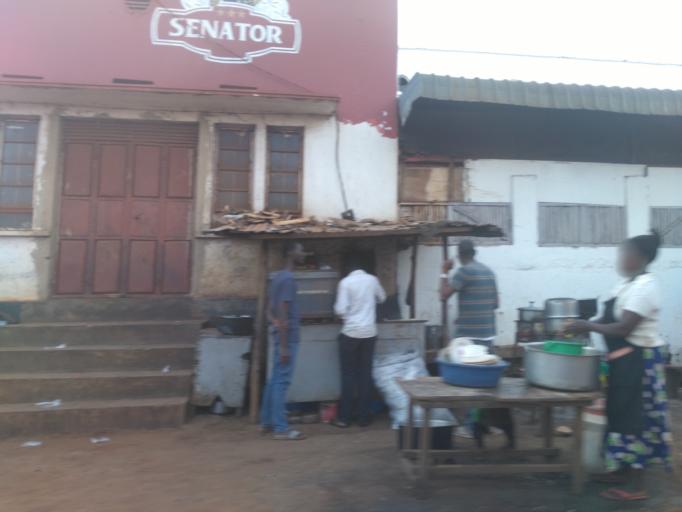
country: UG
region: Eastern Region
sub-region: Jinja District
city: Jinja
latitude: 0.4261
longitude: 33.2124
